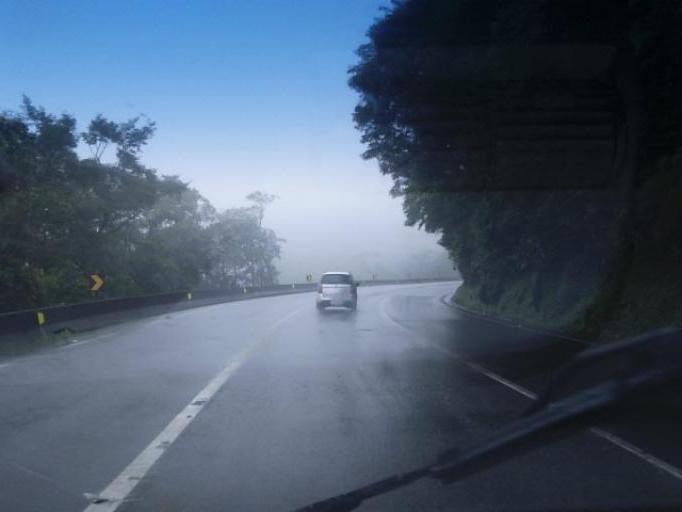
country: BR
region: Parana
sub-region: Guaratuba
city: Guaratuba
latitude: -25.8604
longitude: -48.9493
